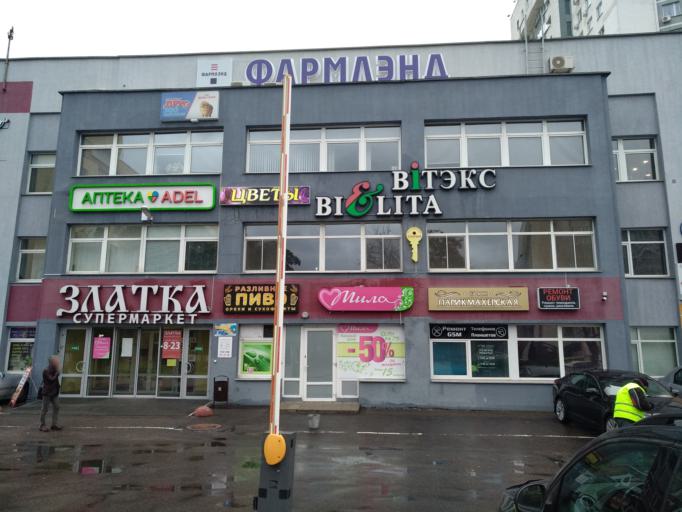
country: BY
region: Minsk
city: Minsk
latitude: 53.9392
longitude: 27.5984
